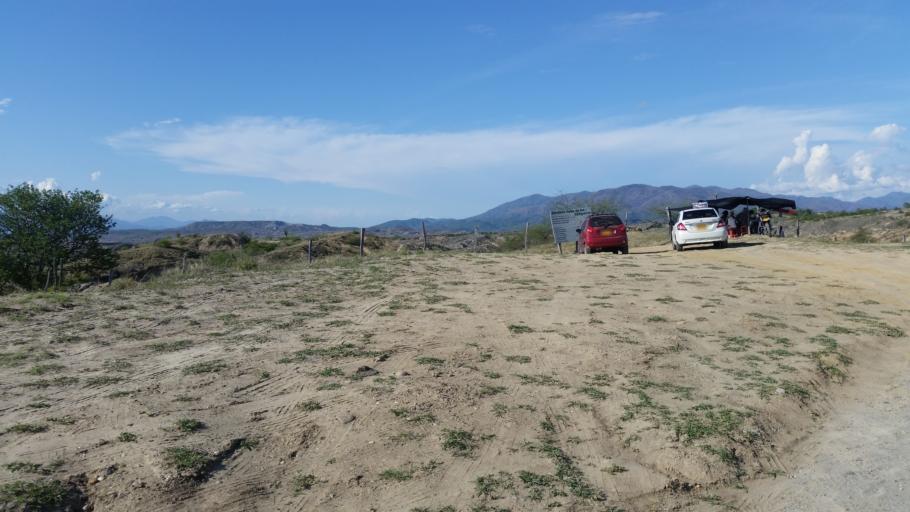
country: CO
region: Huila
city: Baraya
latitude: 3.2366
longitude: -75.1015
